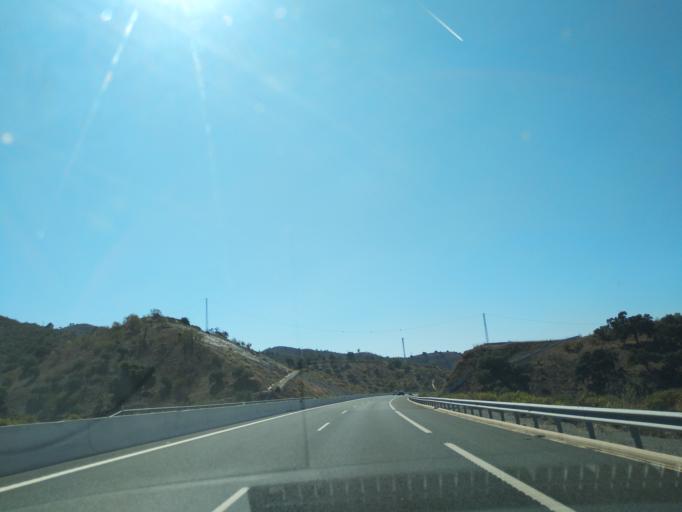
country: ES
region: Andalusia
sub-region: Provincia de Malaga
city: Almogia
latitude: 36.7973
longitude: -4.4669
